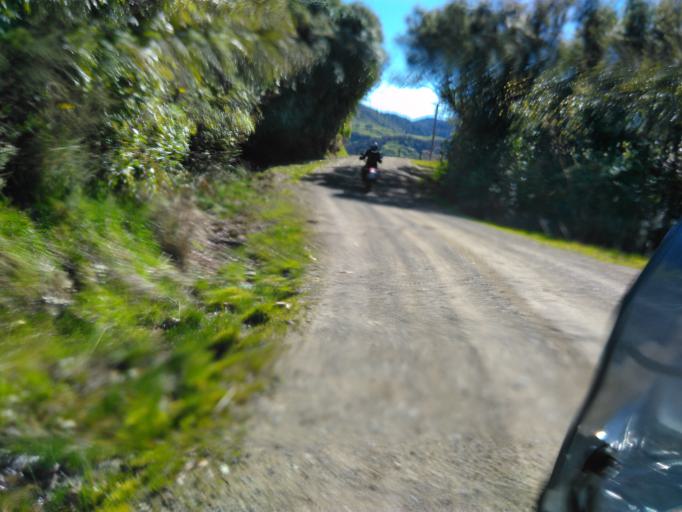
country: NZ
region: Bay of Plenty
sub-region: Opotiki District
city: Opotiki
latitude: -38.3566
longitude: 177.5896
